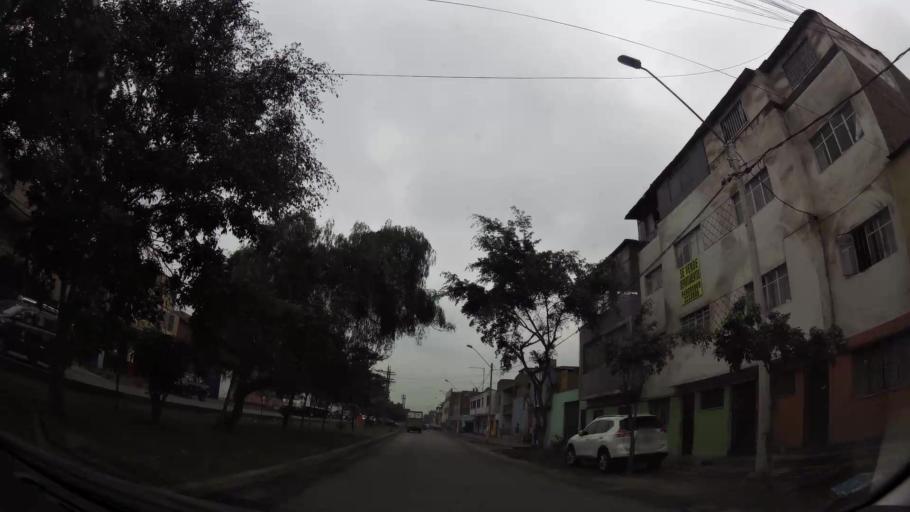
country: PE
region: Lima
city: Lima
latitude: -12.0667
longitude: -77.0200
